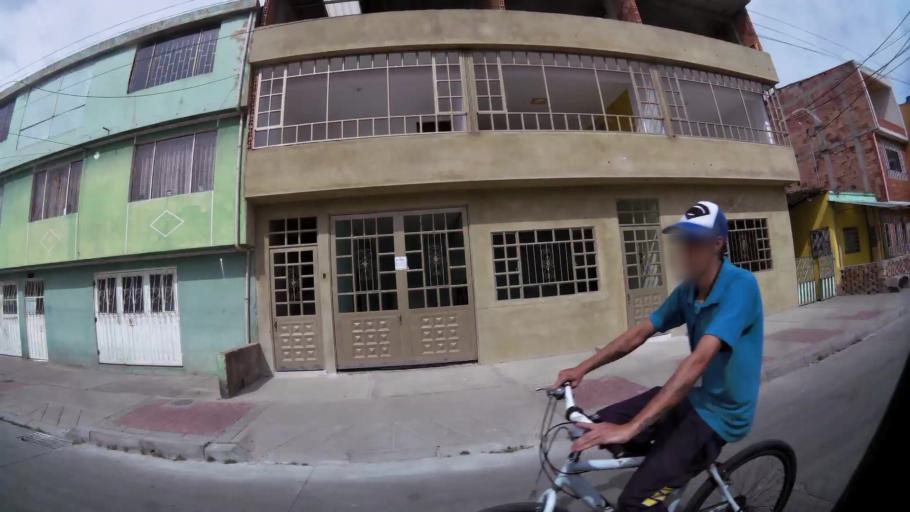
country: CO
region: Cundinamarca
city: Funza
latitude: 4.7093
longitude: -74.2034
